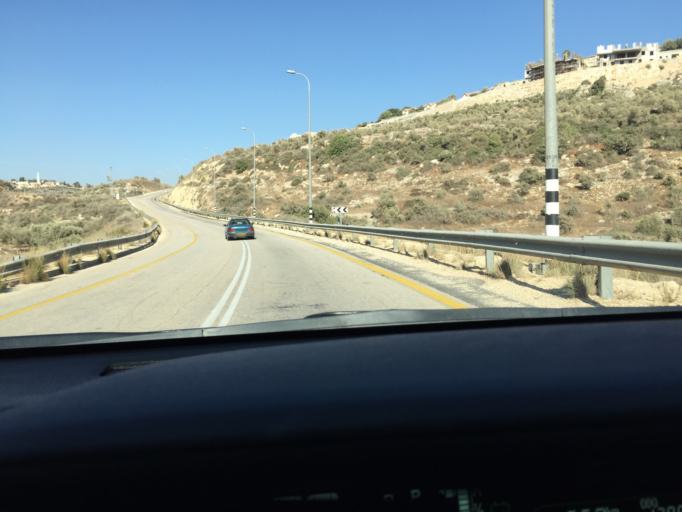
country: PS
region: West Bank
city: Rafat
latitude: 32.0648
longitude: 35.0492
